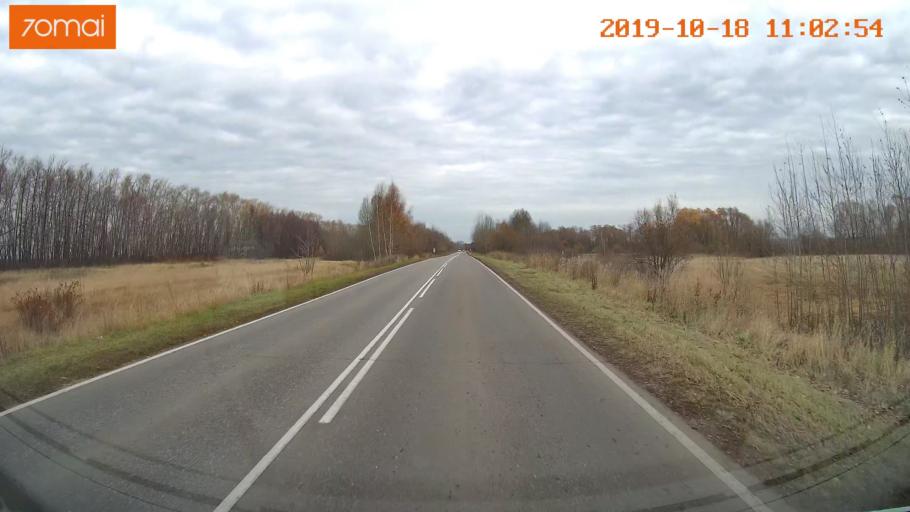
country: RU
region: Tula
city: Yepifan'
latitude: 53.8721
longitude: 38.5442
